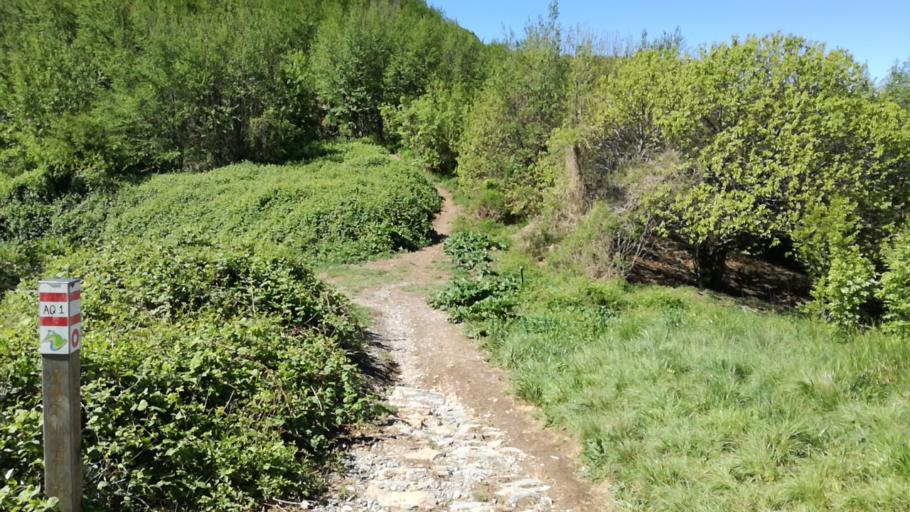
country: IT
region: Liguria
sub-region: Provincia di Genova
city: Manesseno
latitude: 44.4592
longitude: 8.9379
